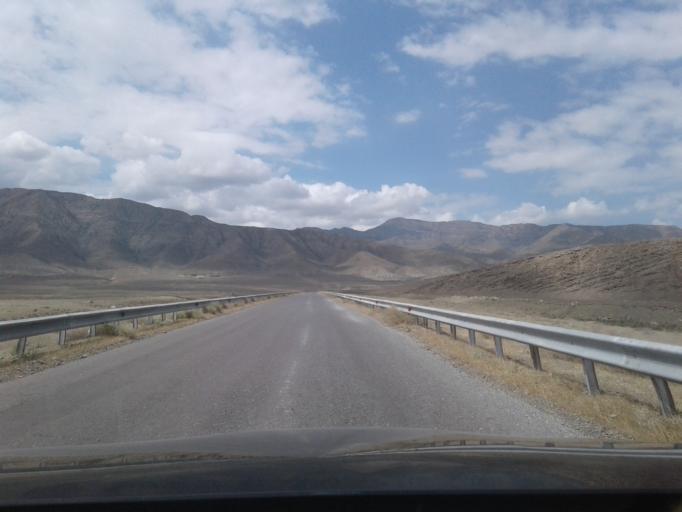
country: TM
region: Ahal
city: Baharly
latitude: 38.5074
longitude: 57.1270
